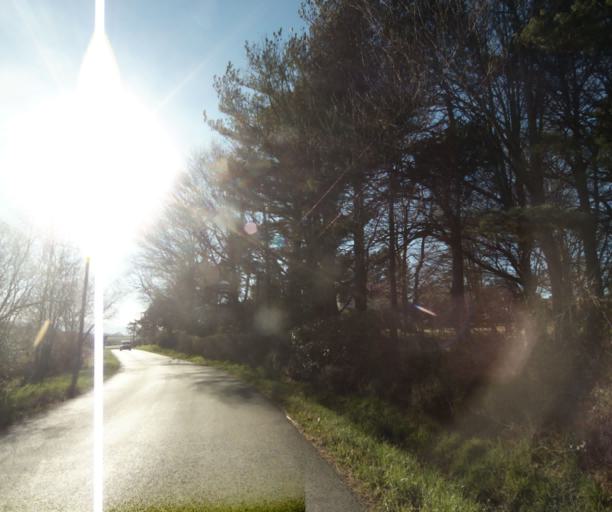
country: FR
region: Aquitaine
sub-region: Departement des Pyrenees-Atlantiques
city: Hendaye
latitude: 43.3566
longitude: -1.7440
